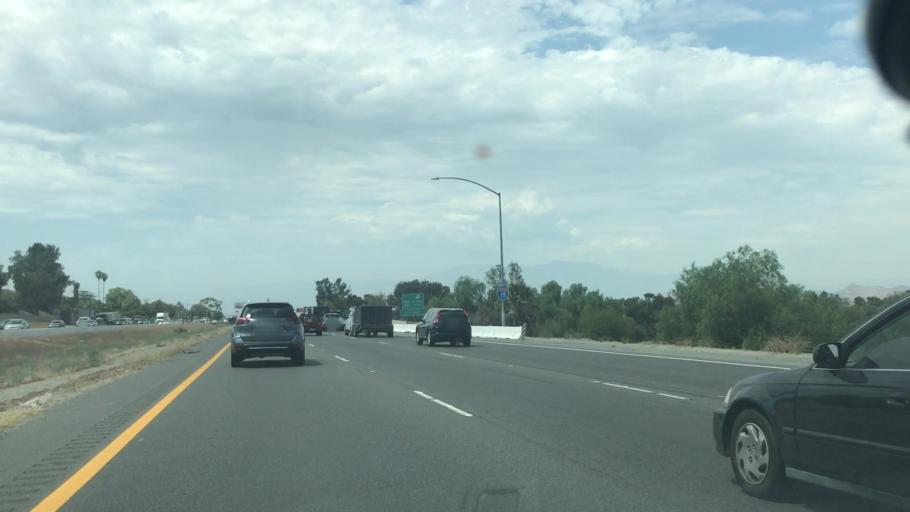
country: US
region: California
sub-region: Riverside County
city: El Cerrito
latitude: 33.8355
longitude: -117.5317
